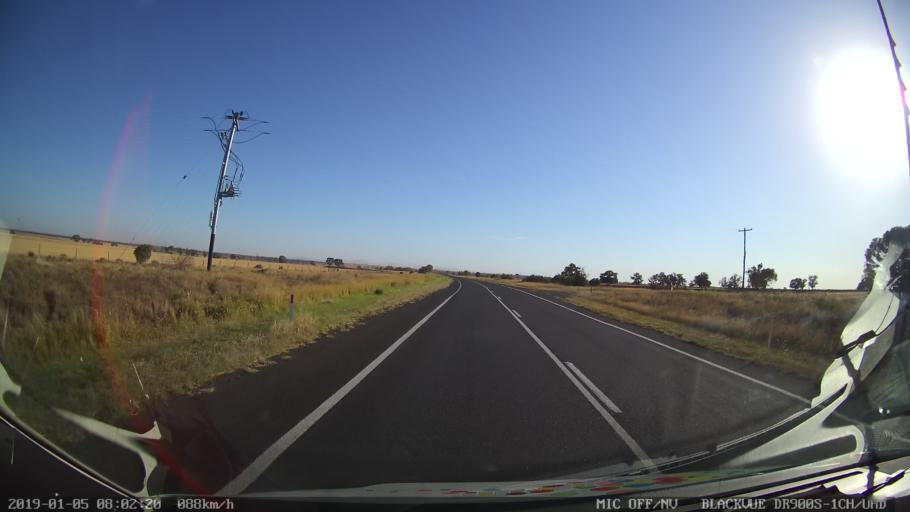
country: AU
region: New South Wales
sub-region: Gilgandra
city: Gilgandra
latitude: -31.6767
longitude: 148.7099
